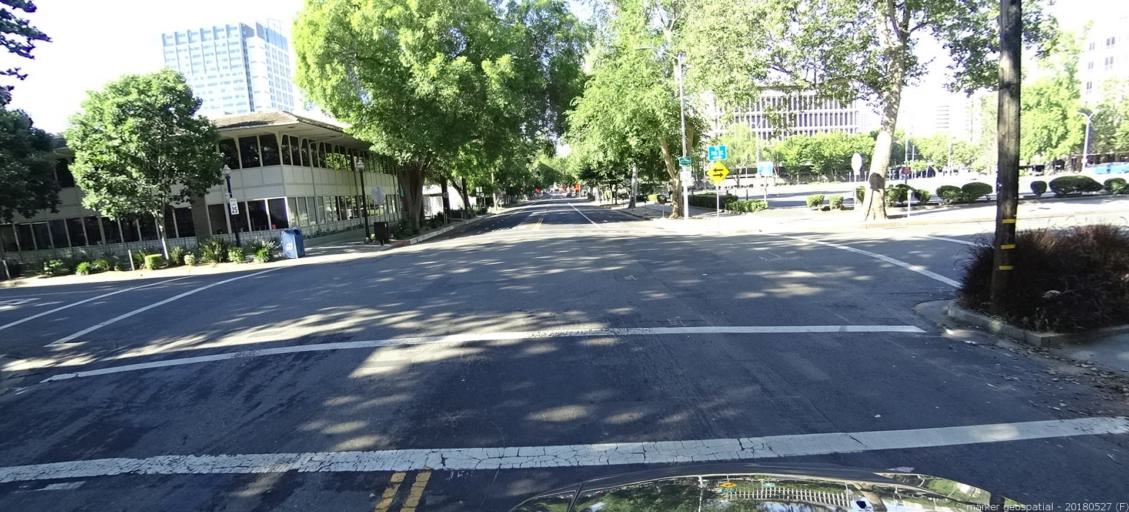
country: US
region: California
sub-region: Sacramento County
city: Sacramento
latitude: 38.5851
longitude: -121.4929
